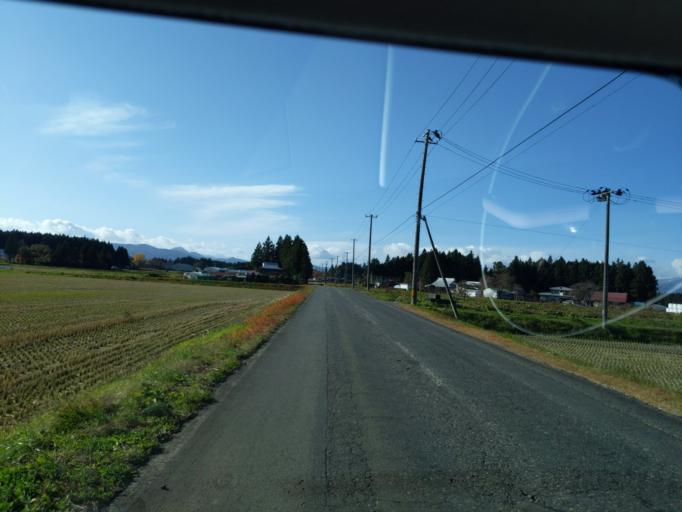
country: JP
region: Iwate
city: Mizusawa
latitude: 39.0857
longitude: 141.0979
